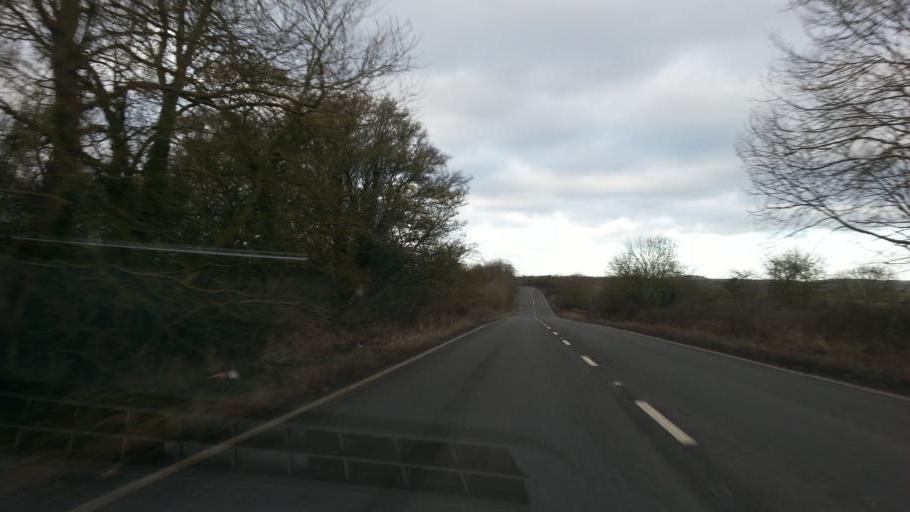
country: GB
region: England
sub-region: Nottinghamshire
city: Farndon
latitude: 53.1231
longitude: -0.8758
